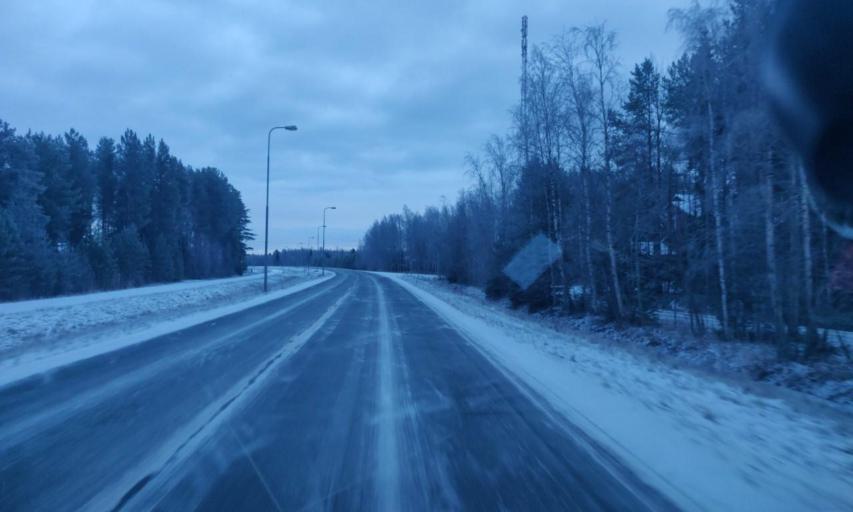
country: FI
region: Northern Ostrobothnia
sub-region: Oulu
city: Oulunsalo
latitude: 64.9759
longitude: 25.2853
